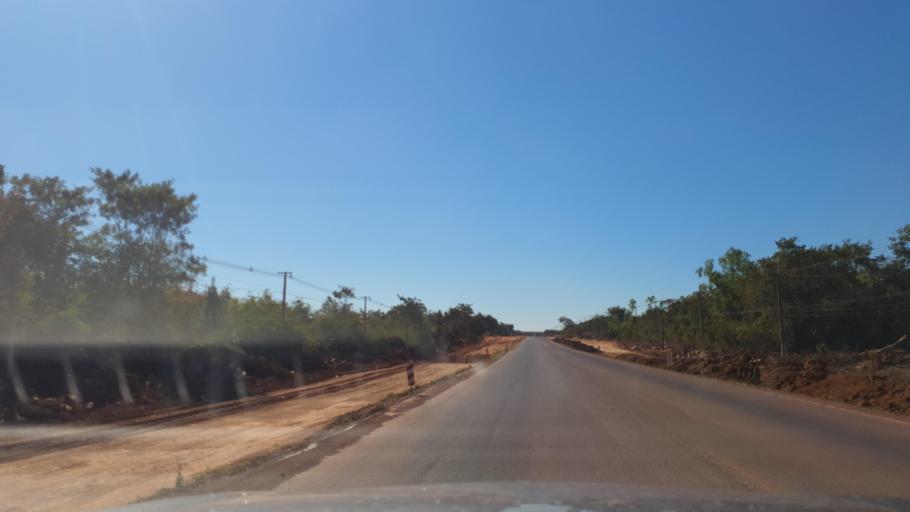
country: TH
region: Nakhon Phanom
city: Ban Phaeng
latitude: 17.8038
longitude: 104.2706
